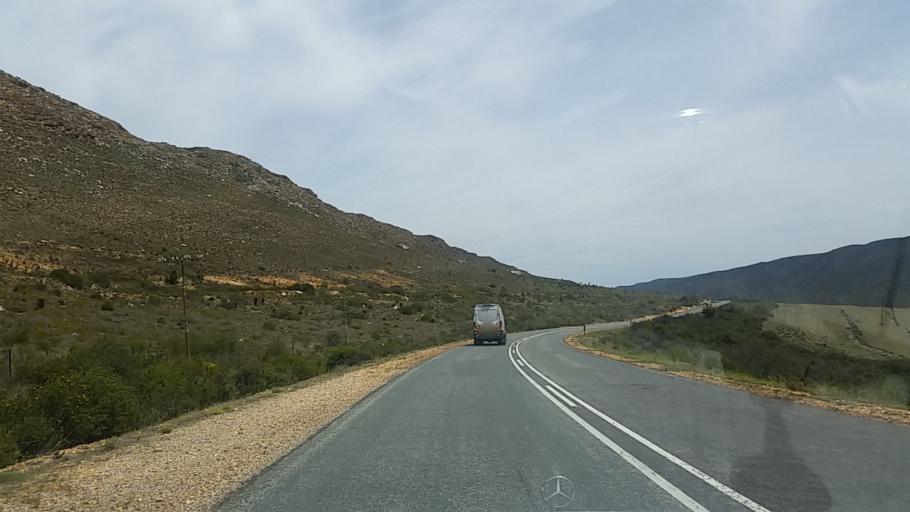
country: ZA
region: Western Cape
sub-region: Eden District Municipality
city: Knysna
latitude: -33.7423
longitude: 23.0312
